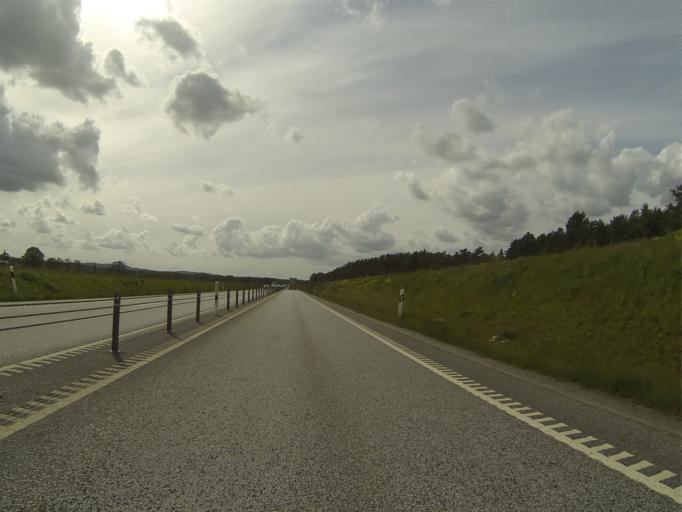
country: SE
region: Skane
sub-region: Sjobo Kommun
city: Blentarp
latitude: 55.6396
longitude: 13.5567
